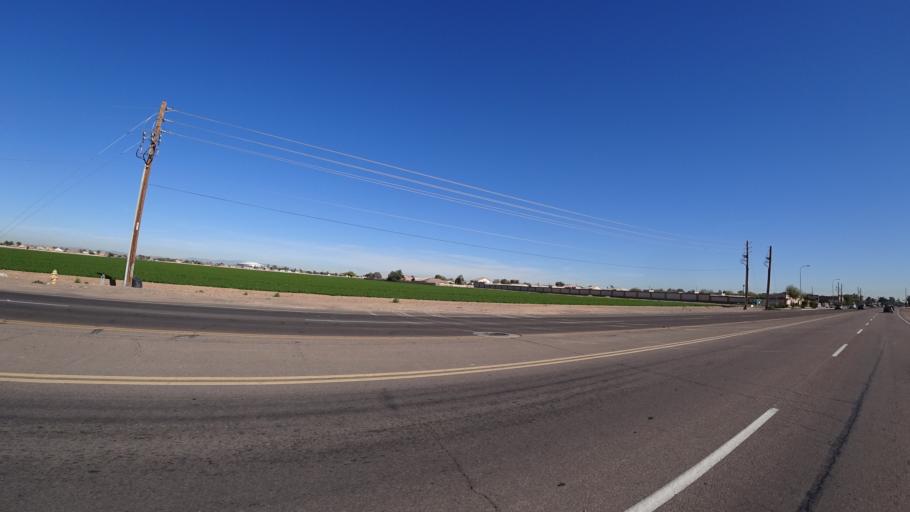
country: US
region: Arizona
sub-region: Maricopa County
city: Tolleson
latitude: 33.4940
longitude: -112.2608
